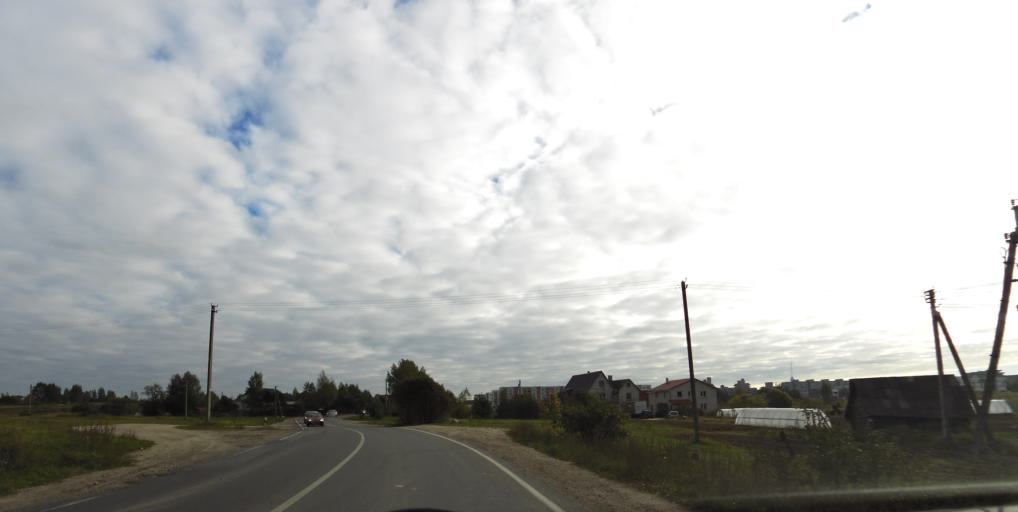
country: LT
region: Vilnius County
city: Pilaite
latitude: 54.7104
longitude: 25.1668
